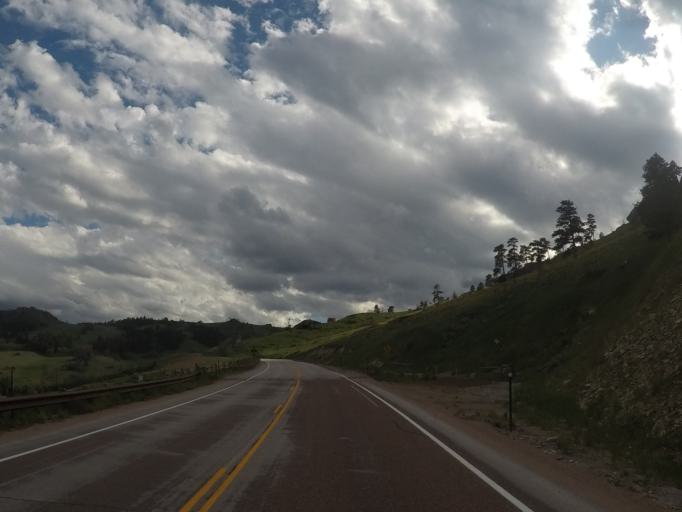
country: US
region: Wyoming
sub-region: Sheridan County
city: Sheridan
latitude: 44.8065
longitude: -107.3507
